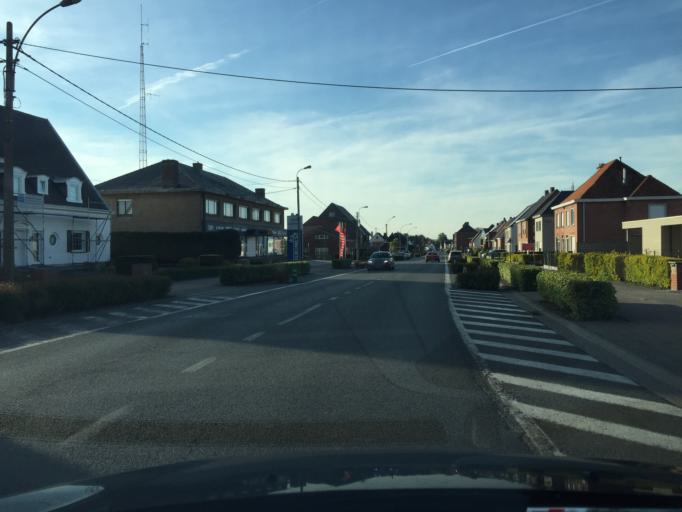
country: BE
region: Flanders
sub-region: Provincie Oost-Vlaanderen
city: Aalter
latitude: 51.0969
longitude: 3.4423
